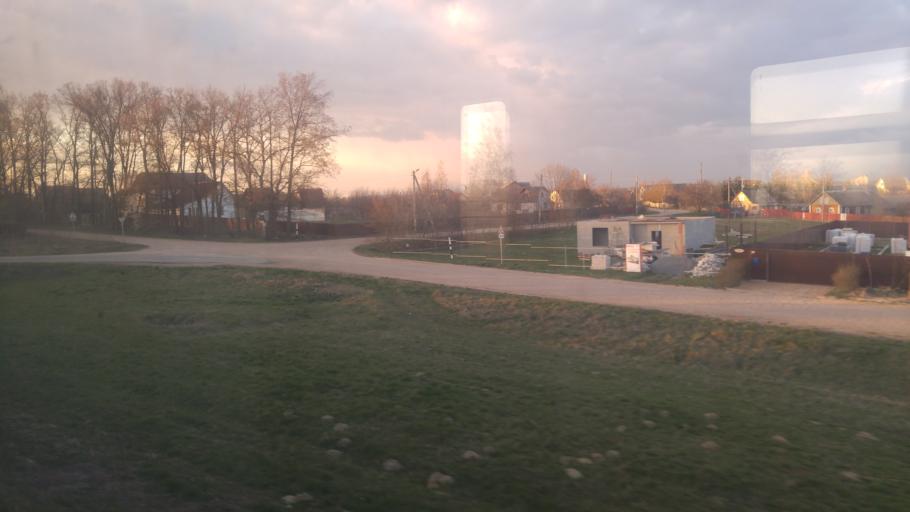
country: BY
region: Minsk
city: Rudzyensk
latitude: 53.6388
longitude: 27.7942
